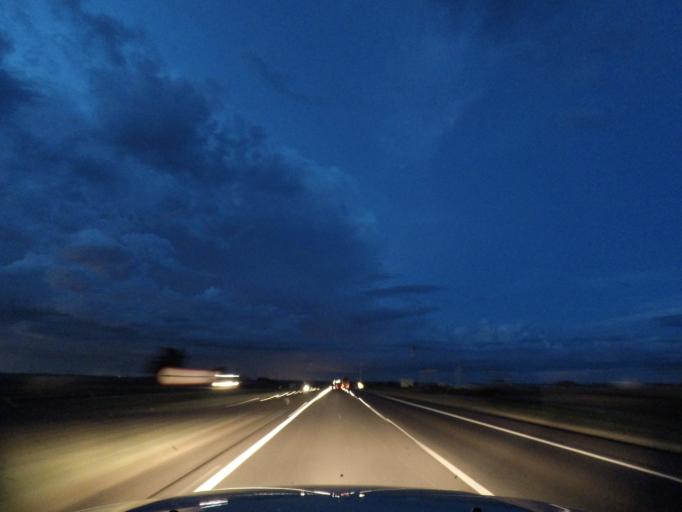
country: BR
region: Minas Gerais
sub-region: Uberlandia
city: Uberlandia
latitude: -19.2263
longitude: -48.1440
